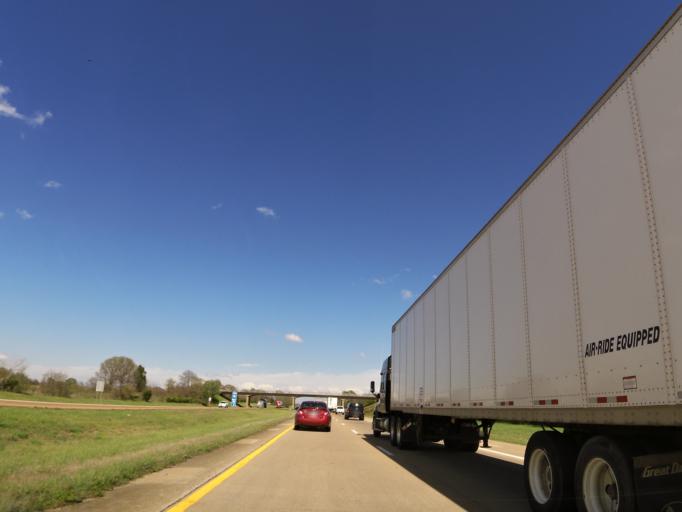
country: US
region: Tennessee
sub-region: Gibson County
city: Medina
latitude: 35.7124
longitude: -88.6522
